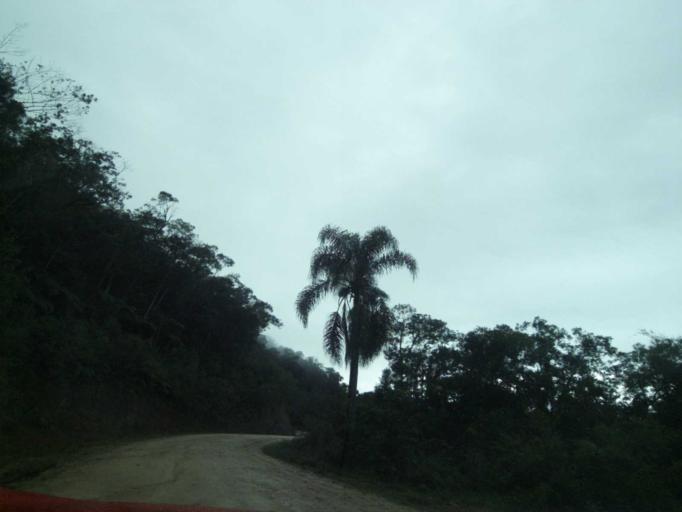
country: BR
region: Santa Catarina
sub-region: Anitapolis
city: Anitapolis
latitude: -27.9186
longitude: -49.1914
